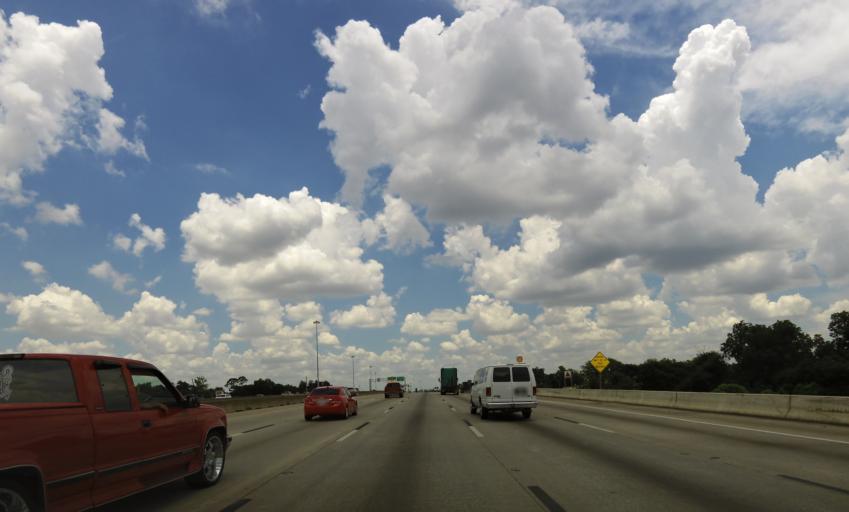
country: US
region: Texas
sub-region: Harris County
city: Houston
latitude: 29.8468
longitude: -95.3333
